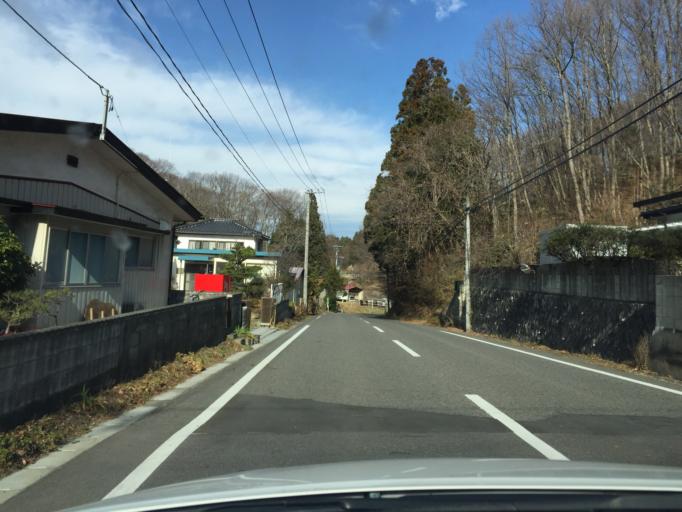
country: JP
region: Fukushima
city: Funehikimachi-funehiki
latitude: 37.2823
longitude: 140.6147
